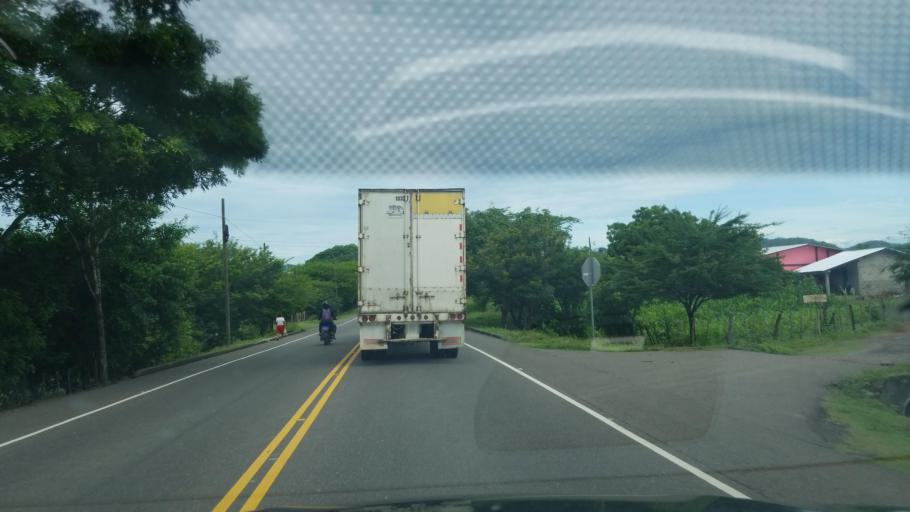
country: HN
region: Valle
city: Goascoran
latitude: 13.5397
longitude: -87.6124
